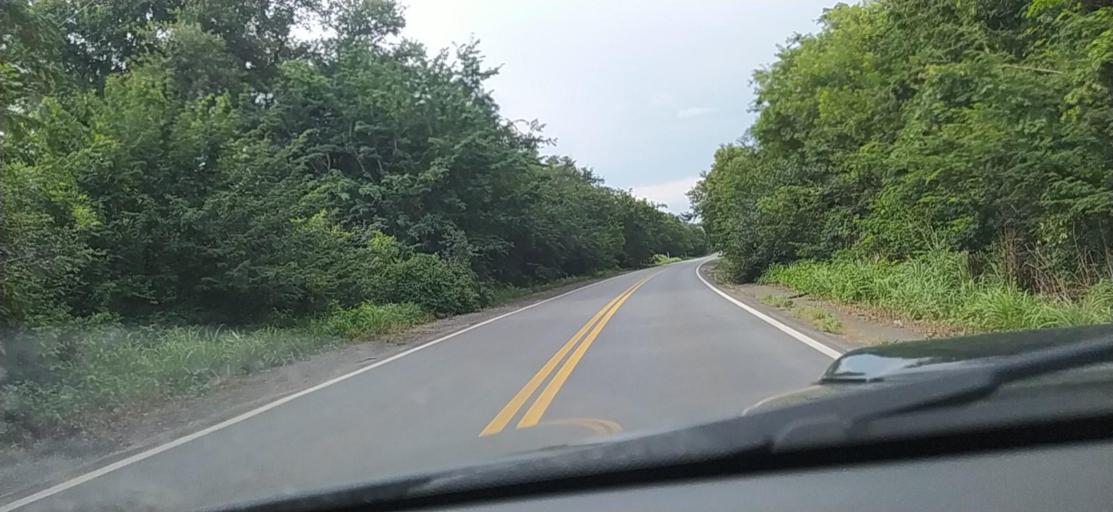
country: BR
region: Minas Gerais
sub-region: Francisco Sa
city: Francisco Sa
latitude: -16.5247
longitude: -43.6803
